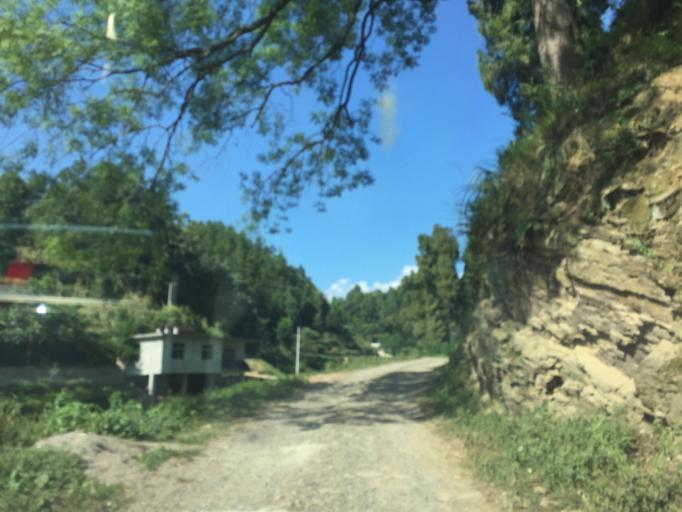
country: CN
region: Guizhou Sheng
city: Jiashi
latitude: 28.3328
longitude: 108.3014
